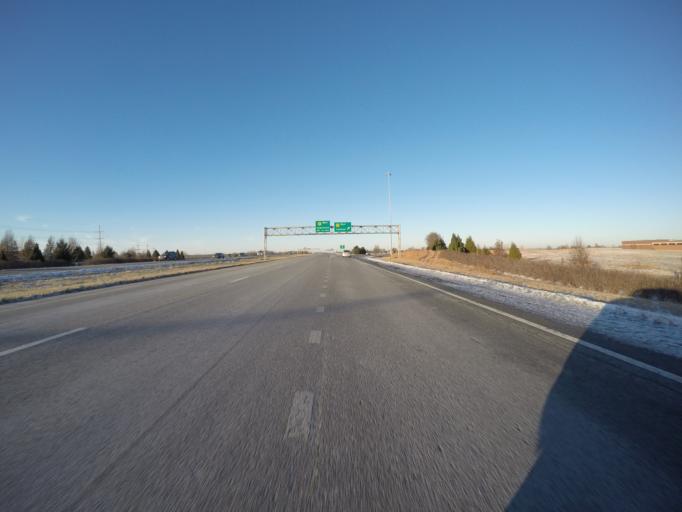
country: US
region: Kansas
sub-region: Johnson County
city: Olathe
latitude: 38.9369
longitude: -94.8525
